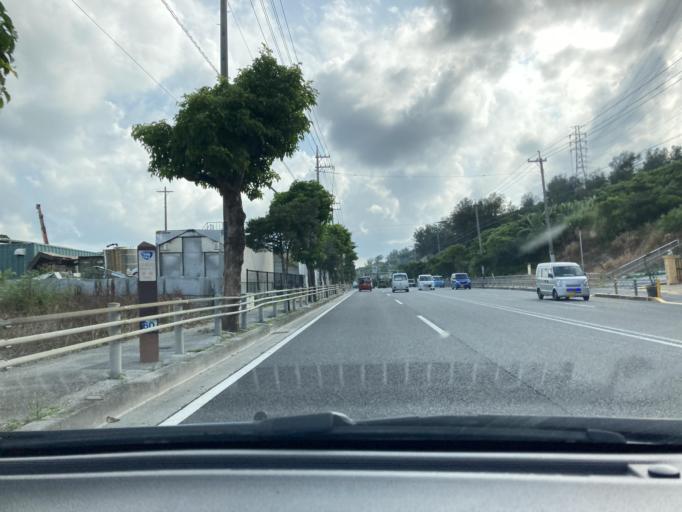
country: JP
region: Okinawa
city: Ginowan
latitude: 26.2521
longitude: 127.7835
